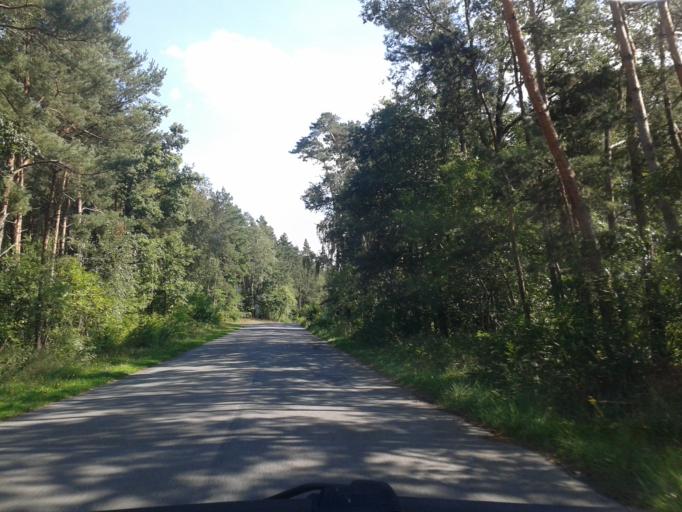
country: DE
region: North Rhine-Westphalia
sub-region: Regierungsbezirk Detmold
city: Augustdorf
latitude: 51.8843
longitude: 8.6927
